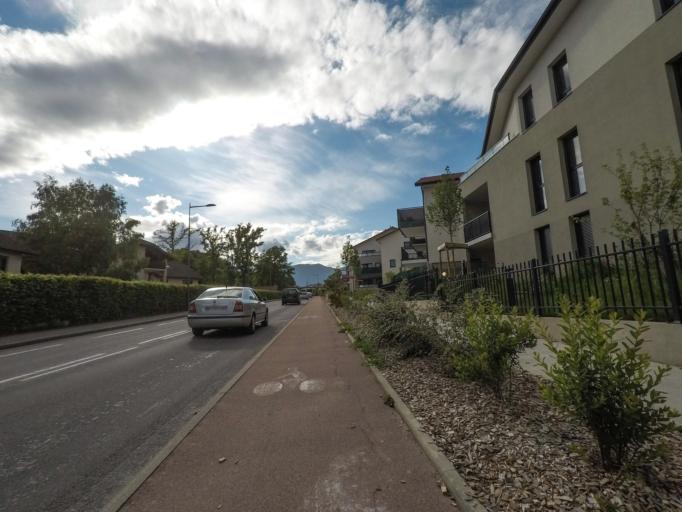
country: CH
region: Geneva
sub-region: Geneva
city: Meyrin
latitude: 46.2554
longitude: 6.0783
